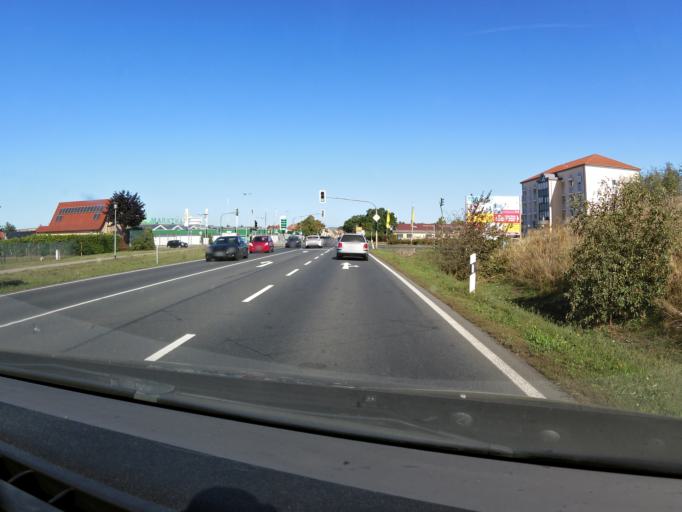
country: DE
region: Thuringia
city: Nordhausen
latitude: 51.4813
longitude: 10.8066
